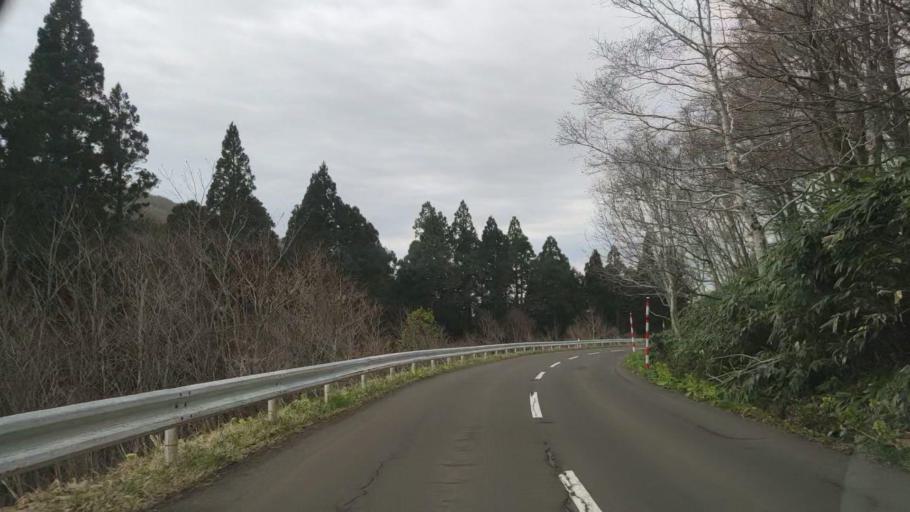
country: JP
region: Akita
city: Hanawa
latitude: 40.4097
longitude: 140.8172
